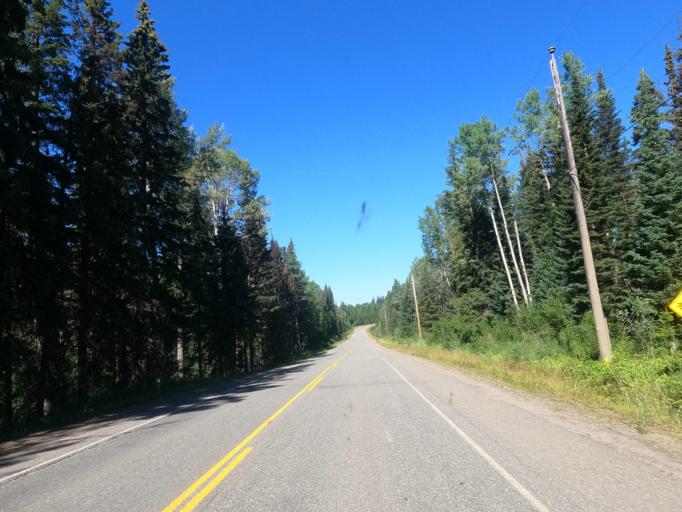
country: CA
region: British Columbia
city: Quesnel
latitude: 53.0196
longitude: -122.0786
